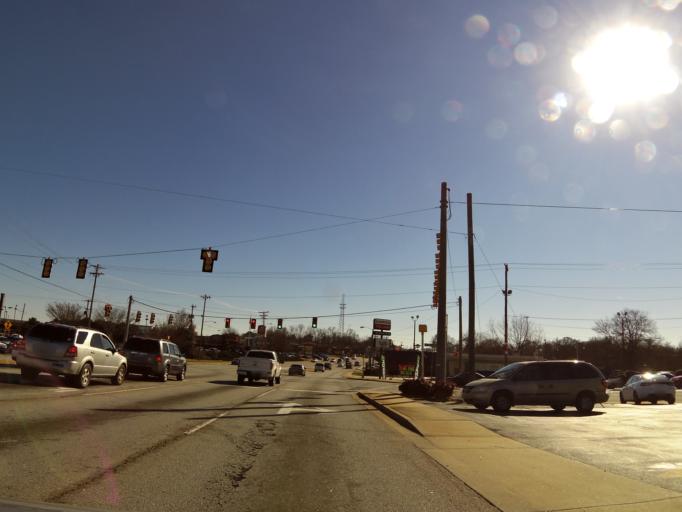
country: US
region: South Carolina
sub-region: Greenville County
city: Sans Souci
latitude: 34.8910
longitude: -82.4064
